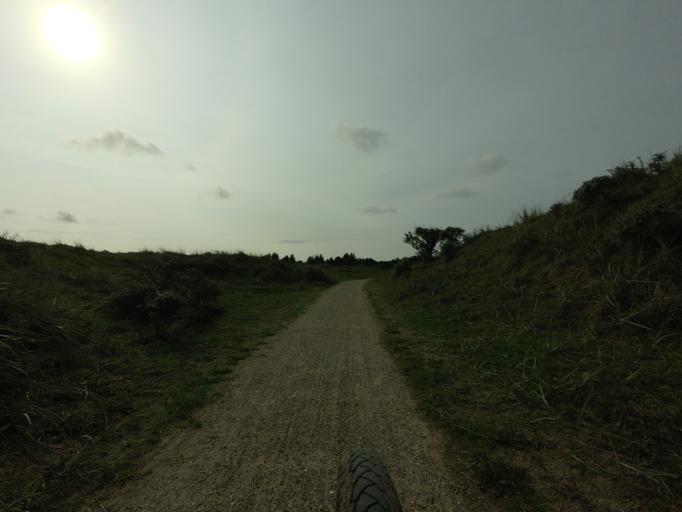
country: DK
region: North Denmark
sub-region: Hjorring Kommune
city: Sindal
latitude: 57.5894
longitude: 10.1477
